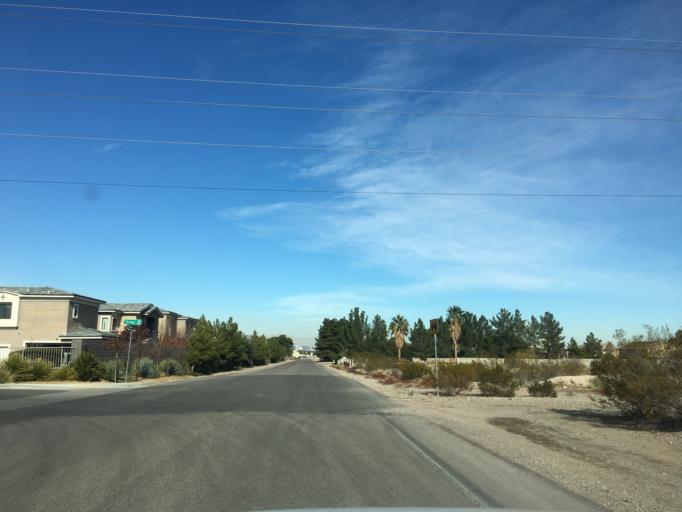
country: US
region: Nevada
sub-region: Clark County
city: Enterprise
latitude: 36.0027
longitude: -115.1682
